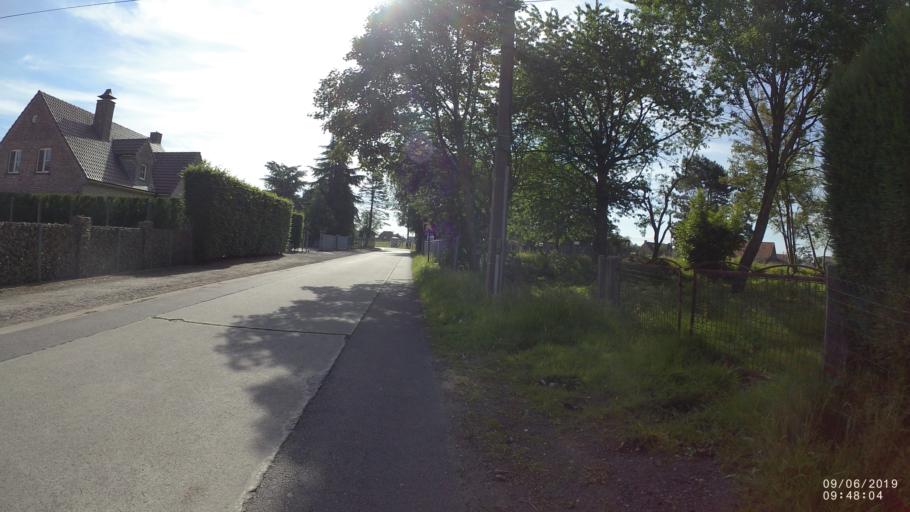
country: BE
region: Flanders
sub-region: Provincie Oost-Vlaanderen
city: Maldegem
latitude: 51.1936
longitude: 3.4822
